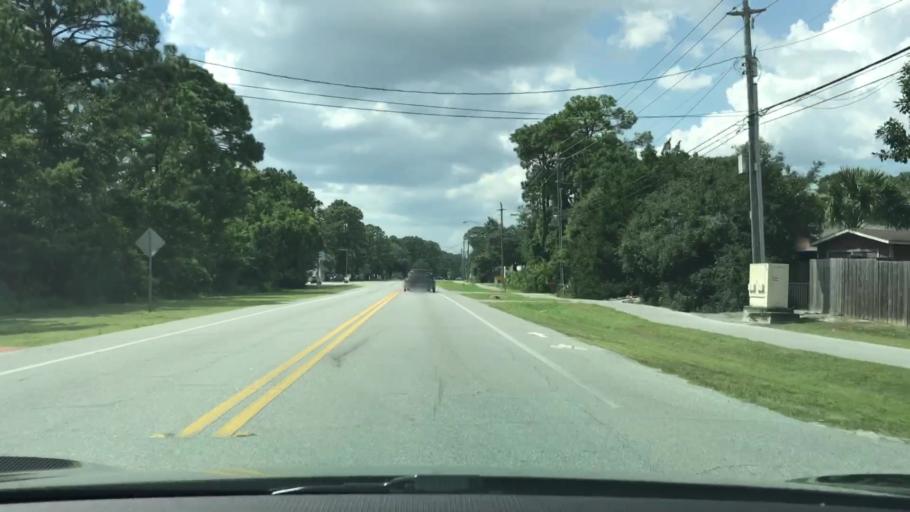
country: US
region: Florida
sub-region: Bay County
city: Lower Grand Lagoon
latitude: 30.1626
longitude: -85.7680
